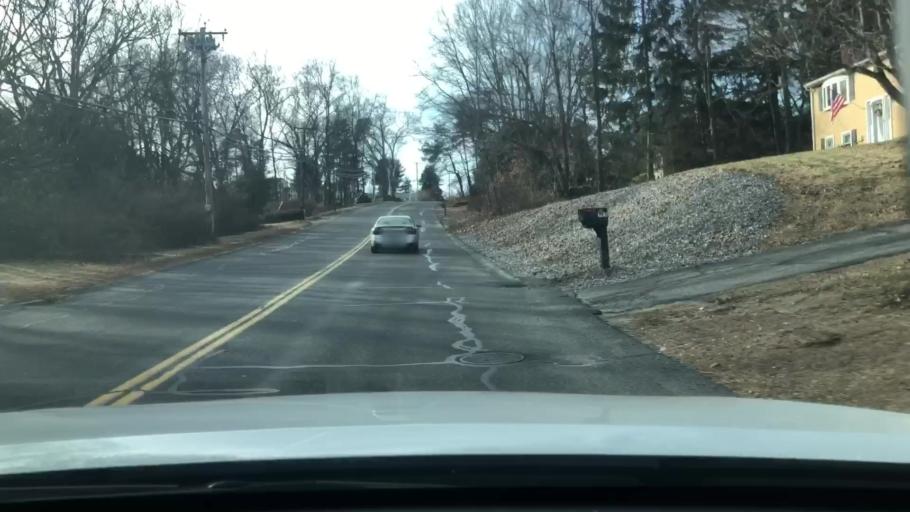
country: US
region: Massachusetts
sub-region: Worcester County
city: Millbury
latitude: 42.1961
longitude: -71.7295
